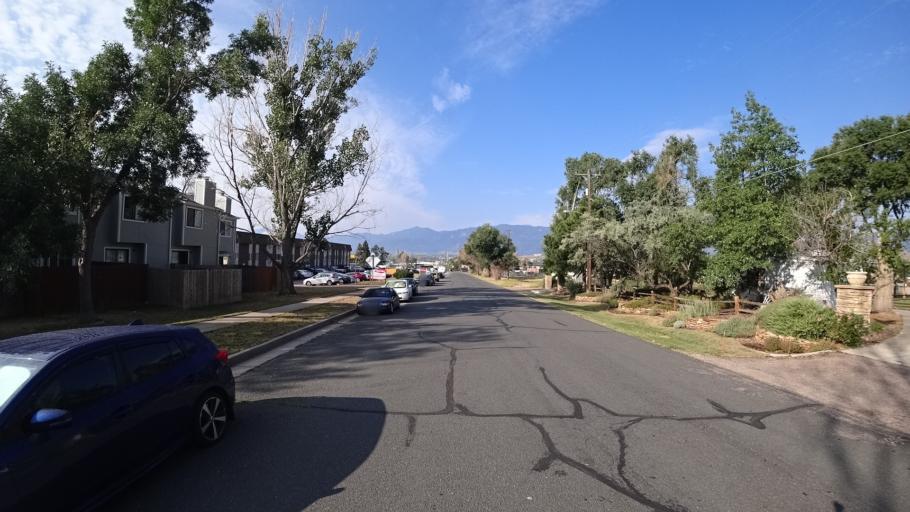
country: US
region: Colorado
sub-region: El Paso County
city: Colorado Springs
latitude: 38.8910
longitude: -104.8134
